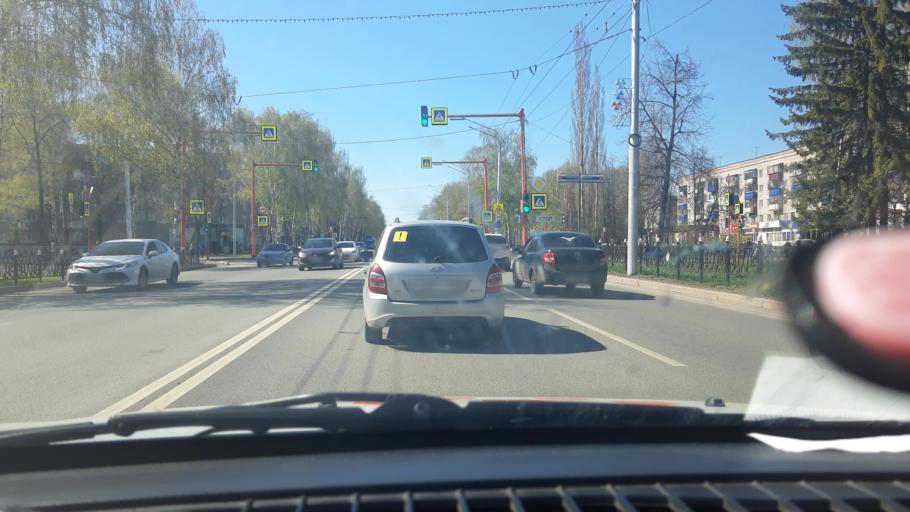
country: RU
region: Bashkortostan
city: Sterlitamak
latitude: 53.6333
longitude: 55.9227
